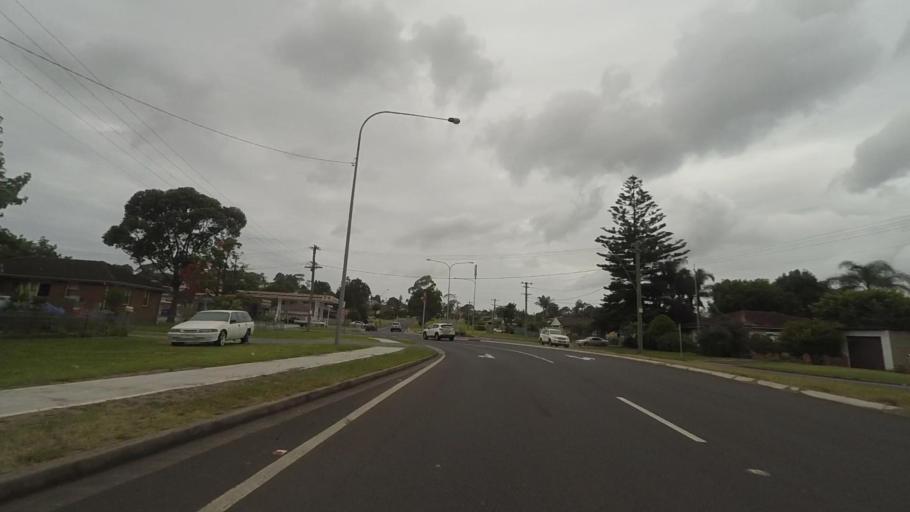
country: AU
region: New South Wales
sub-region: Wollongong
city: Berkeley
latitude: -34.4767
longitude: 150.8384
